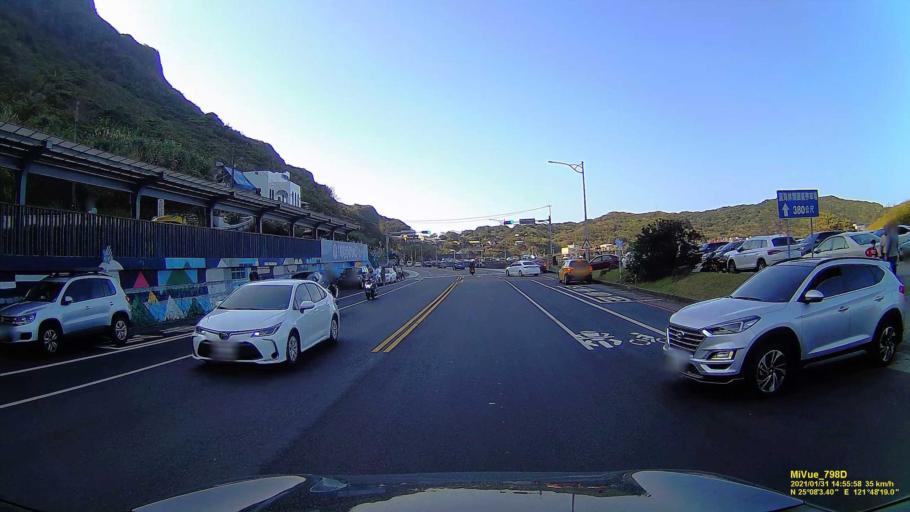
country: TW
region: Taiwan
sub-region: Keelung
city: Keelung
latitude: 25.1344
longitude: 121.8051
